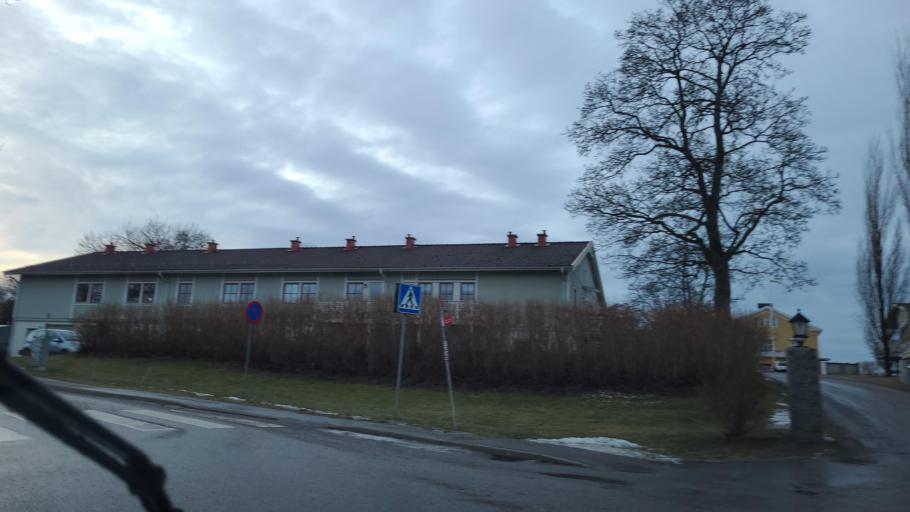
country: SE
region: Stockholm
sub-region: Vallentuna Kommun
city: Vallentuna
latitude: 59.5185
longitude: 18.0632
